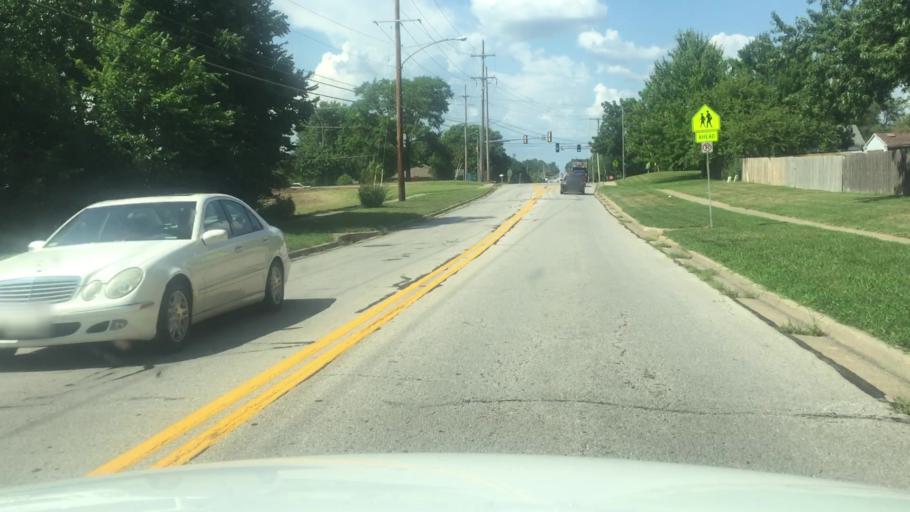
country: US
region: Kansas
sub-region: Johnson County
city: Shawnee
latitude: 39.0061
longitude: -94.7424
